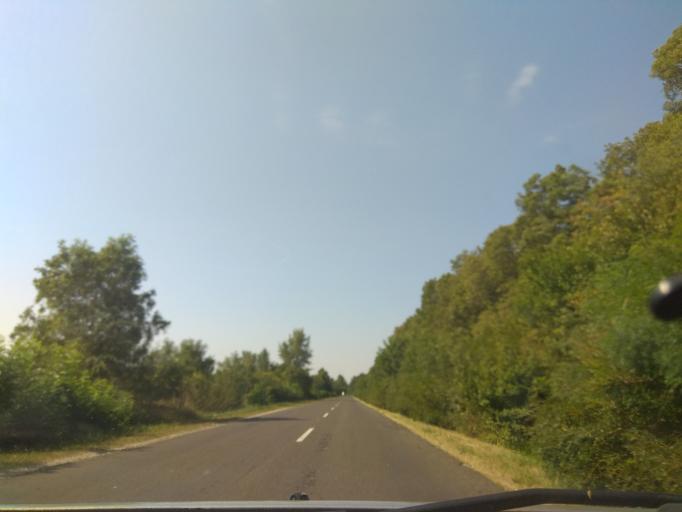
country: HU
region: Borsod-Abauj-Zemplen
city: Harsany
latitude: 47.9254
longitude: 20.7245
